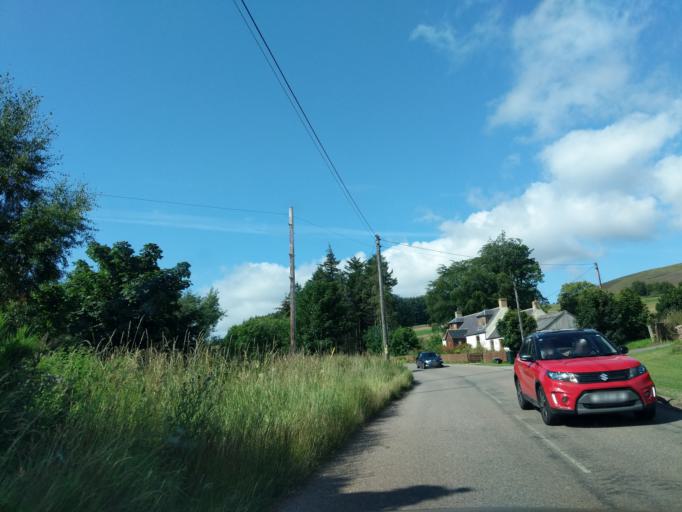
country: GB
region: Scotland
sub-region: Moray
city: Dufftown
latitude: 57.3916
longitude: -3.2107
